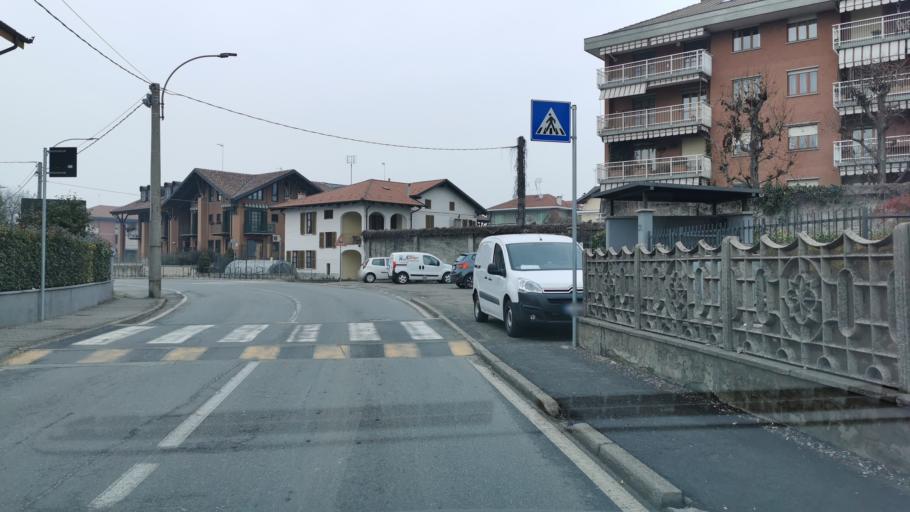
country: IT
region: Piedmont
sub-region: Provincia di Torino
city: San Mauro Torinese
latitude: 45.1056
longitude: 7.7614
